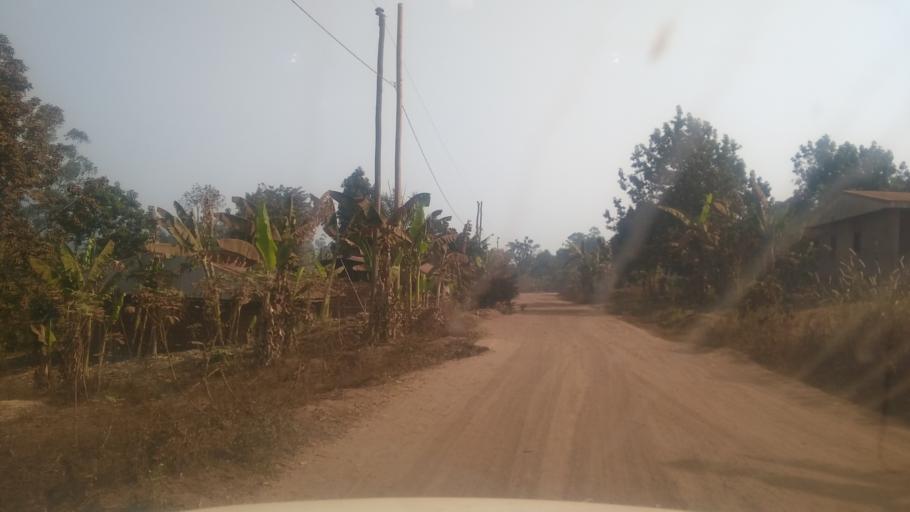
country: CM
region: West
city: Bafoussam
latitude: 5.5192
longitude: 10.4114
